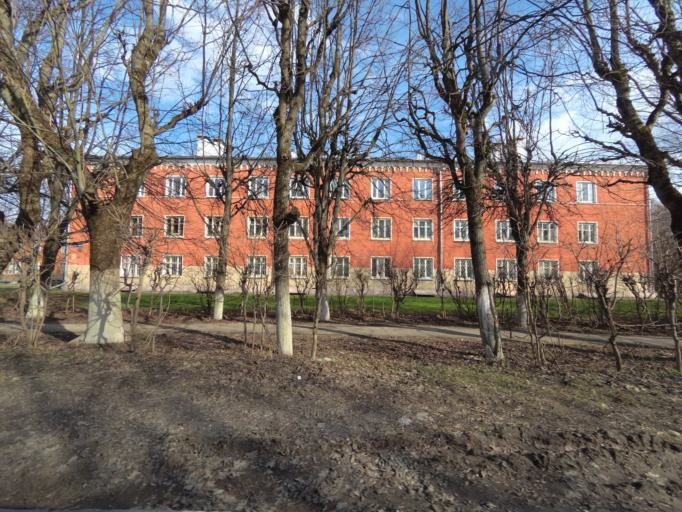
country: RU
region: Moskovskaya
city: Lugovaya
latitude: 56.0447
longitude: 37.4824
